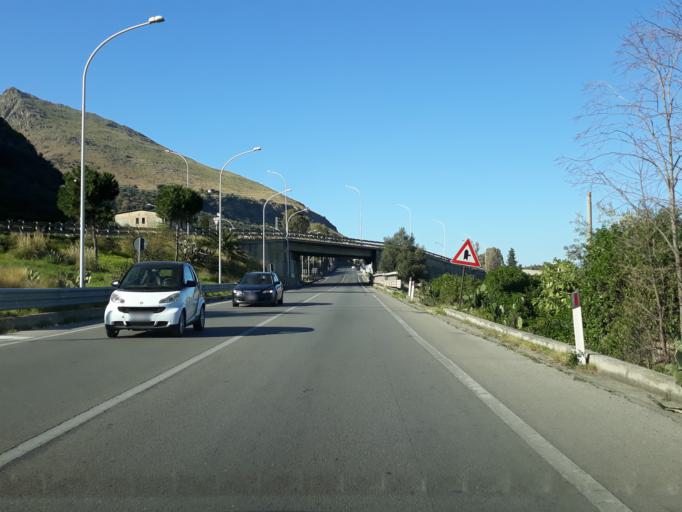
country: IT
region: Sicily
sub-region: Palermo
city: Misilmeri
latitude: 38.0423
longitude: 13.4608
